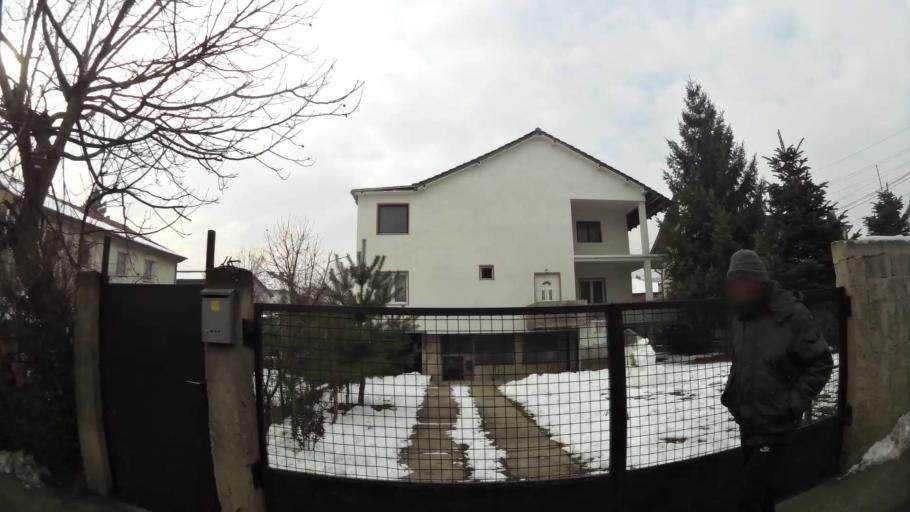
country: MK
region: Saraj
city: Saraj
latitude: 42.0218
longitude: 21.3509
